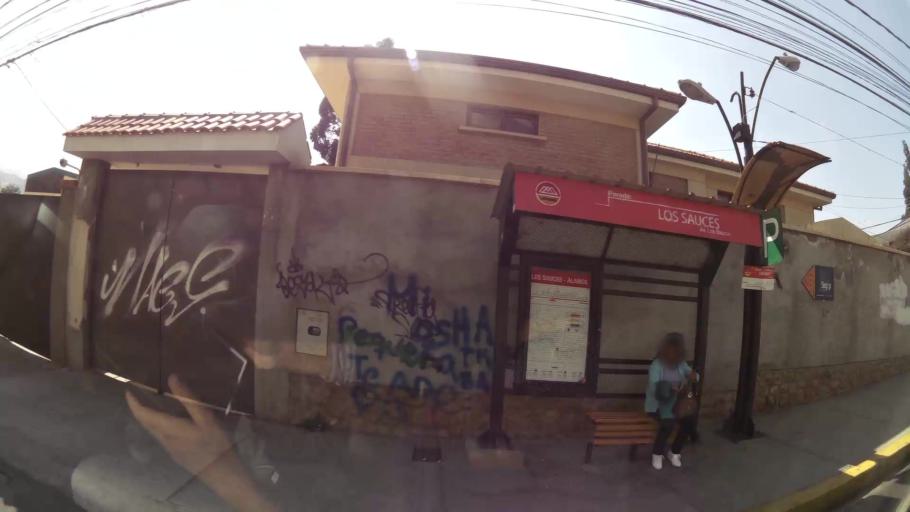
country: BO
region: La Paz
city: La Paz
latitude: -16.5451
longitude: -68.0906
